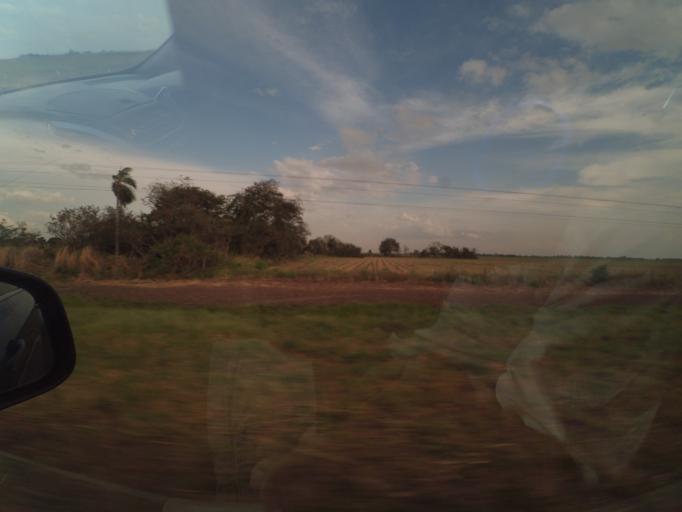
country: BO
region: Santa Cruz
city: Okinawa Numero Uno
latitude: -17.2389
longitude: -62.9694
